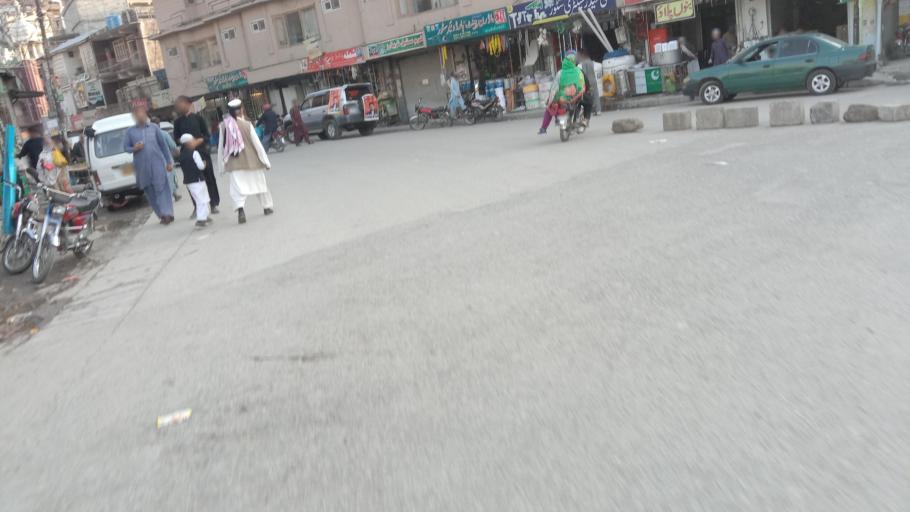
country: PK
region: Khyber Pakhtunkhwa
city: Abbottabad
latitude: 34.1415
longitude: 73.2136
